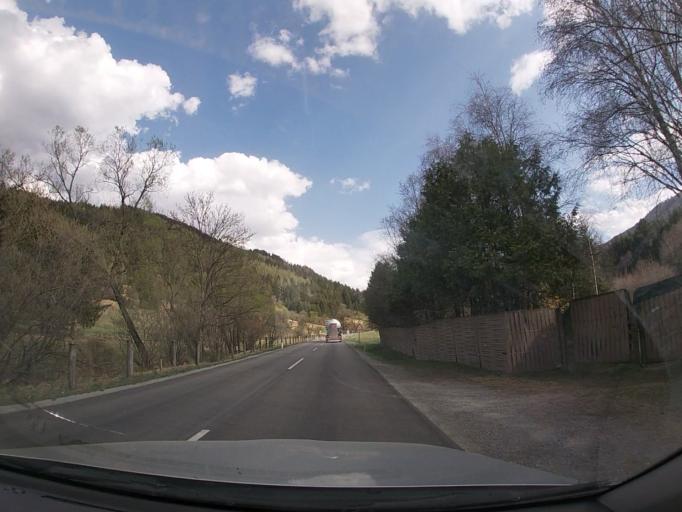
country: AT
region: Styria
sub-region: Politischer Bezirk Murau
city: Sankt Lorenzen bei Scheifling
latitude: 47.1379
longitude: 14.4305
